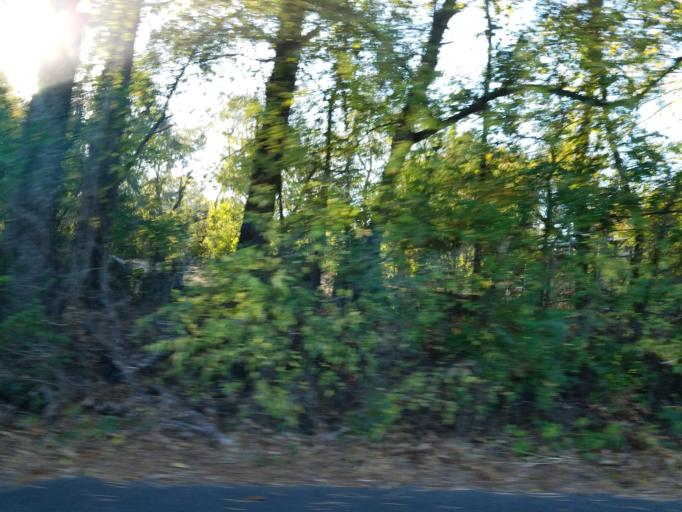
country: US
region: Georgia
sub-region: Bartow County
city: Euharlee
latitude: 34.2341
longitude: -84.9409
